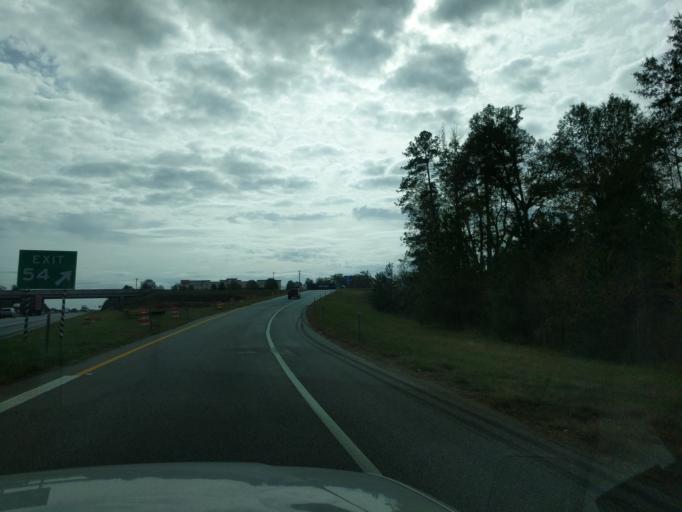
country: US
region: South Carolina
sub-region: Laurens County
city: Clinton
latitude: 34.4990
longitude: -81.8470
